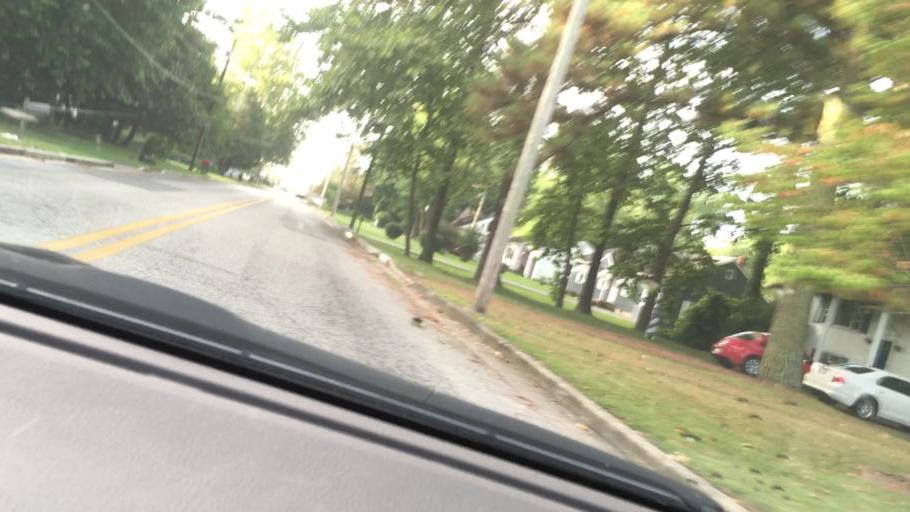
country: US
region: Maryland
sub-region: Wicomico County
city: Fruitland
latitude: 38.3300
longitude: -75.6252
